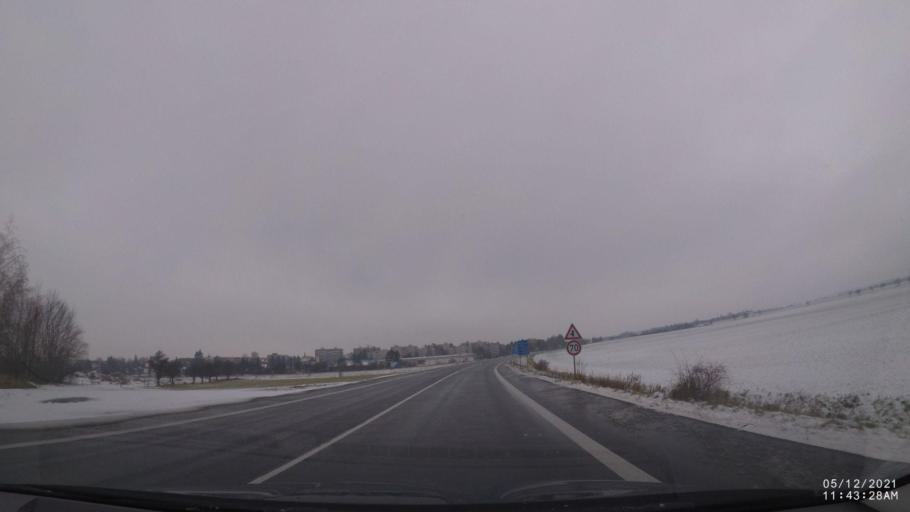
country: CZ
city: Dobruska
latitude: 50.2866
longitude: 16.1712
